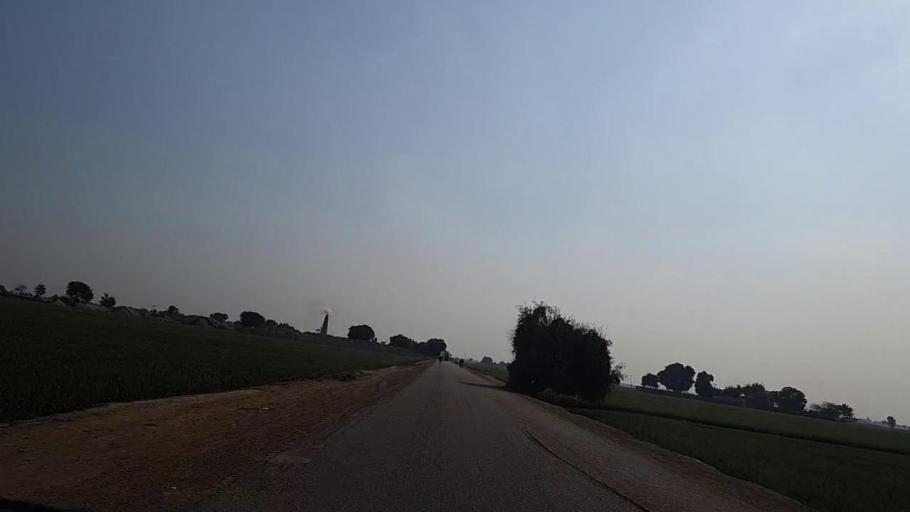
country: PK
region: Sindh
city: Sakrand
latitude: 26.1021
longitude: 68.2908
